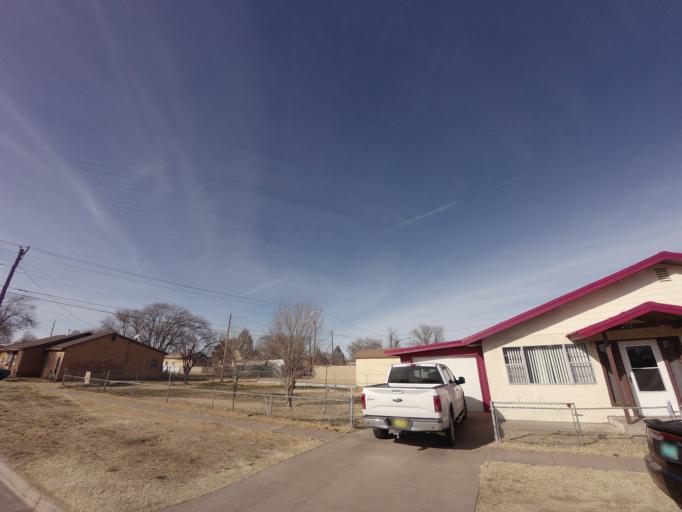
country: US
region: New Mexico
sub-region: Curry County
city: Clovis
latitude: 34.4018
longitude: -103.2196
